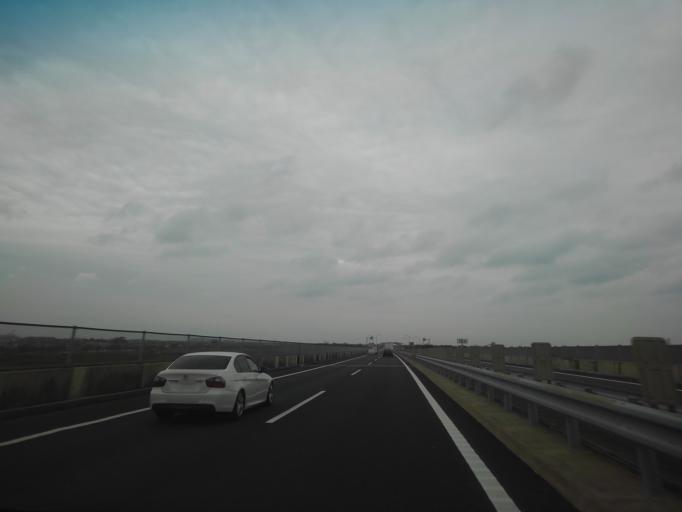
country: JP
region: Chiba
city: Kisarazu
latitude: 35.4140
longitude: 139.9538
